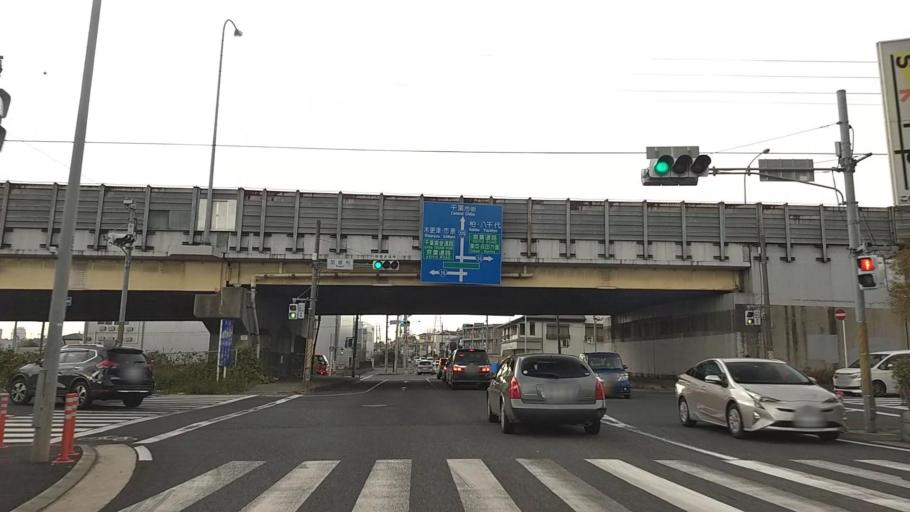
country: JP
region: Chiba
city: Chiba
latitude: 35.6083
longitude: 140.1528
